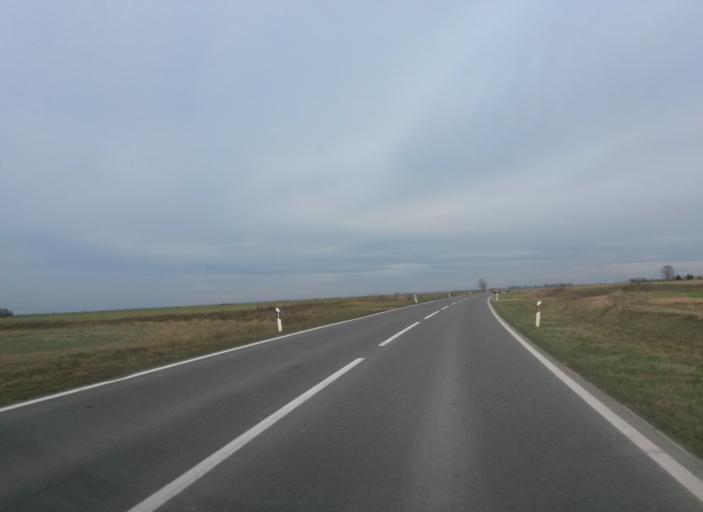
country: HR
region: Osjecko-Baranjska
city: Cepin
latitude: 45.5217
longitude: 18.5379
